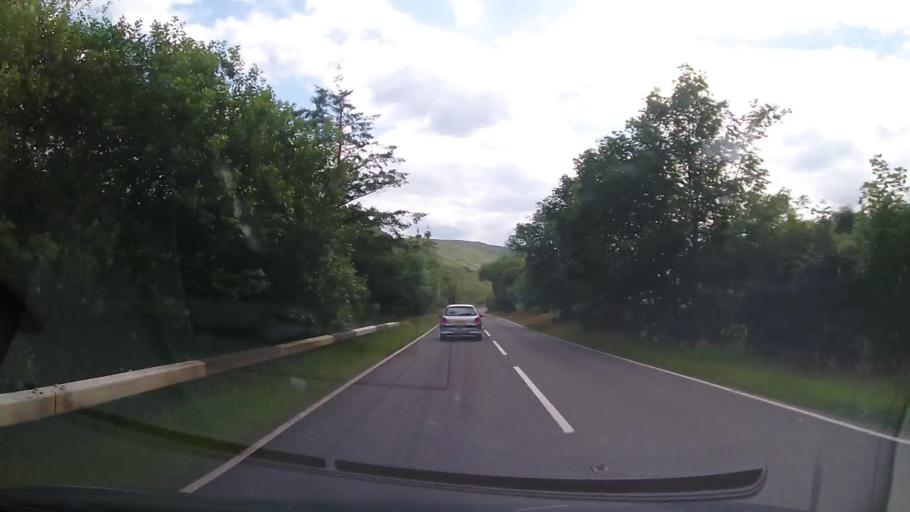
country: GB
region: Wales
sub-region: Gwynedd
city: Trawsfynydd
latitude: 52.9271
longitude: -3.8205
